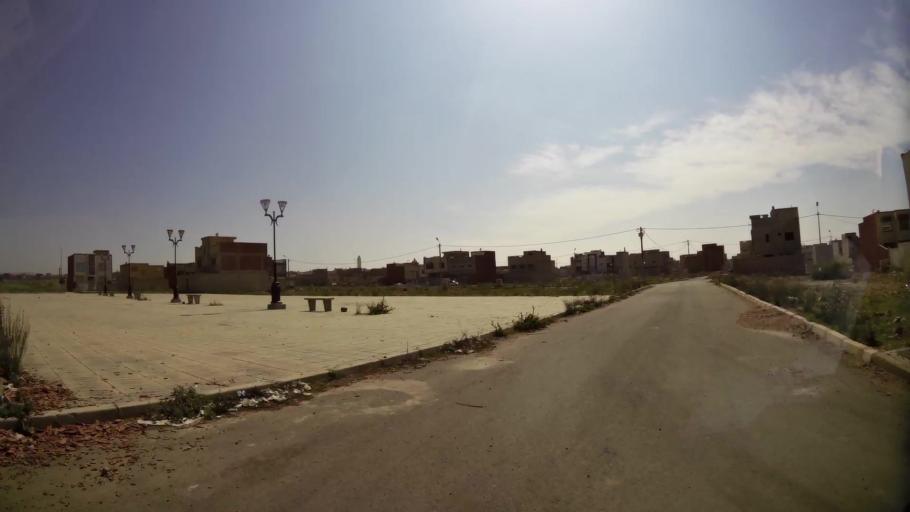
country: MA
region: Oriental
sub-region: Oujda-Angad
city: Oujda
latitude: 34.6965
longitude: -1.8677
